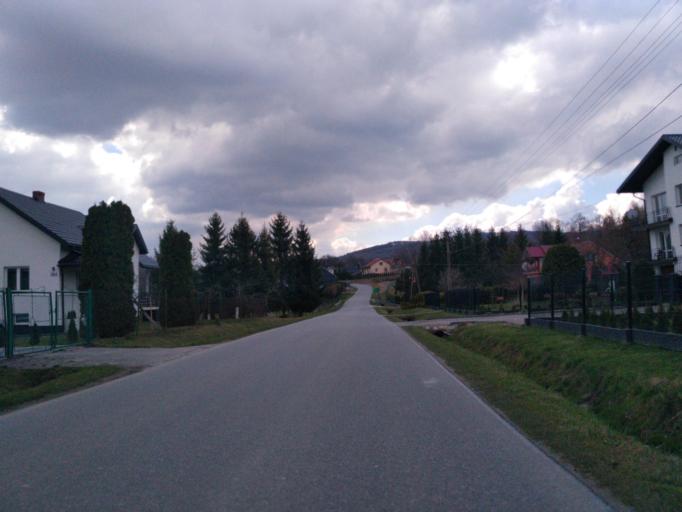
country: PL
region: Subcarpathian Voivodeship
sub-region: Powiat brzozowski
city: Dydnia
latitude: 49.6778
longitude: 22.1842
